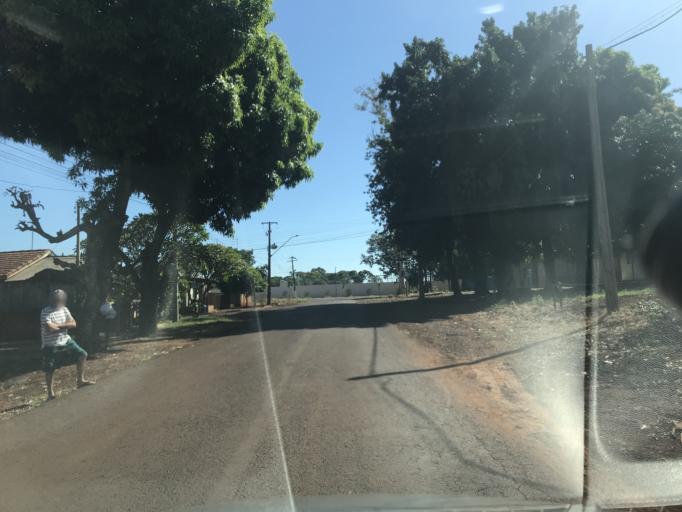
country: BR
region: Parana
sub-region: Palotina
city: Palotina
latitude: -24.2657
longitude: -53.8343
